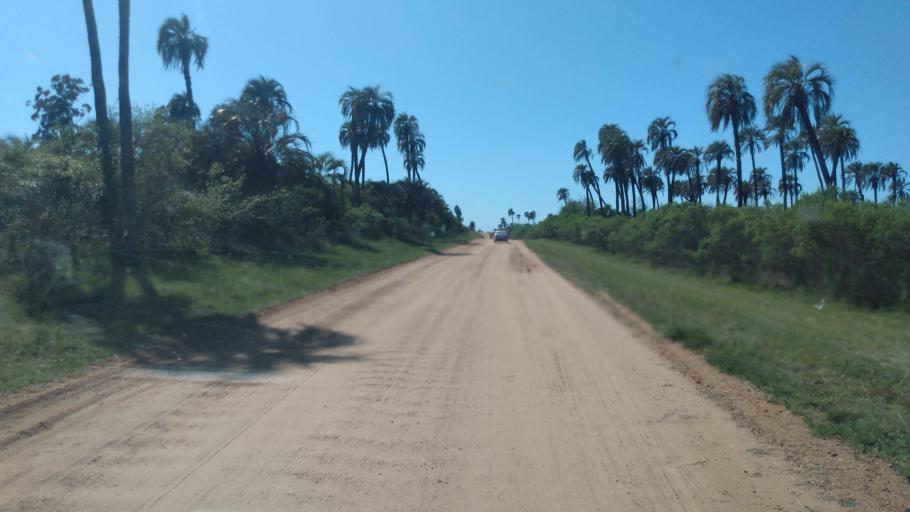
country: AR
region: Entre Rios
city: Ubajay
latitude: -31.8538
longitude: -58.2930
